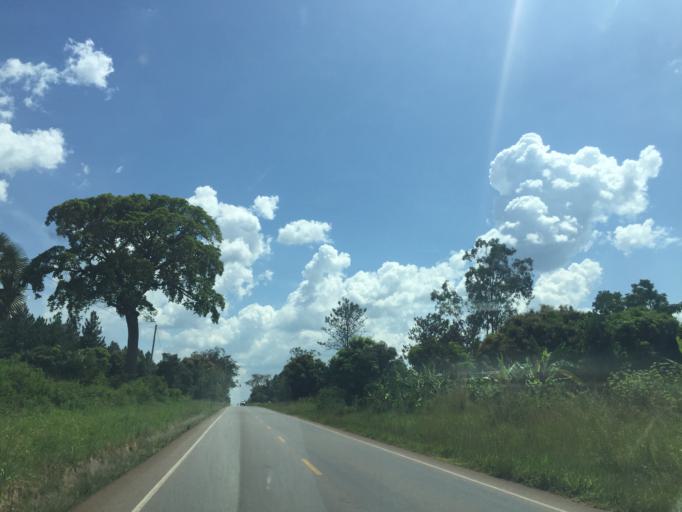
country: UG
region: Central Region
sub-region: Nakasongola District
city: Nakasongola
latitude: 1.2016
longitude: 32.4629
